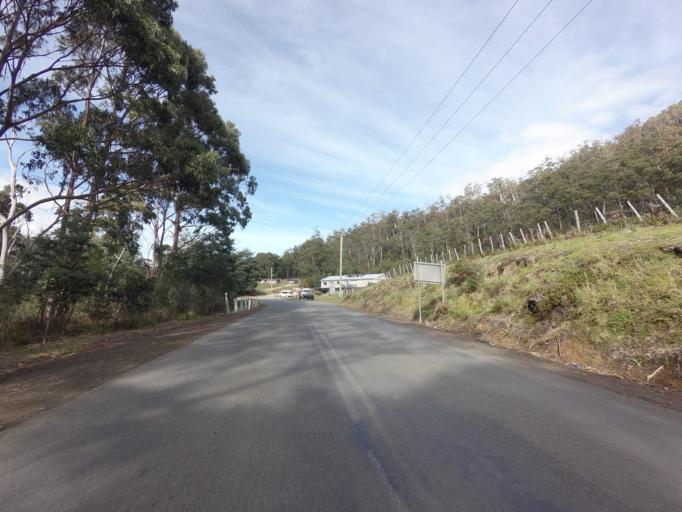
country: AU
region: Tasmania
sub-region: Clarence
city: Sandford
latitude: -43.1145
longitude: 147.7523
